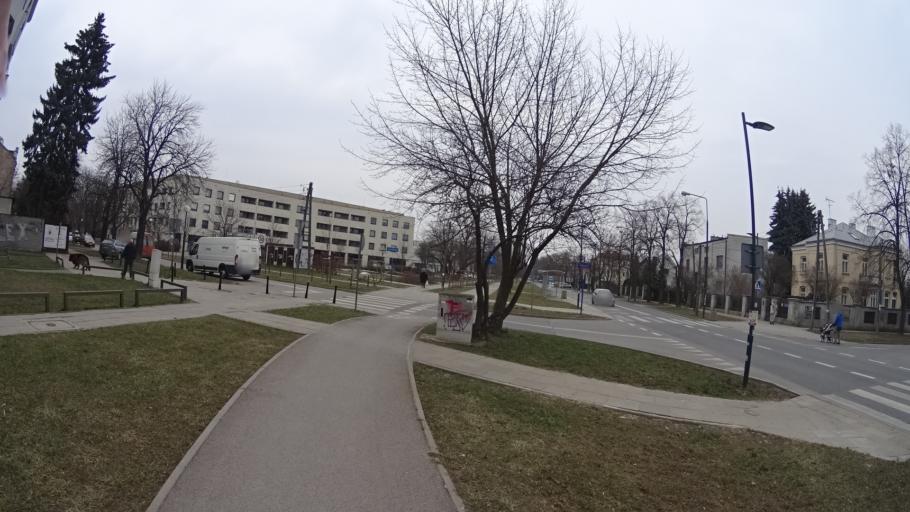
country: PL
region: Masovian Voivodeship
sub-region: Warszawa
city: Ursus
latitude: 52.2076
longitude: 20.9053
